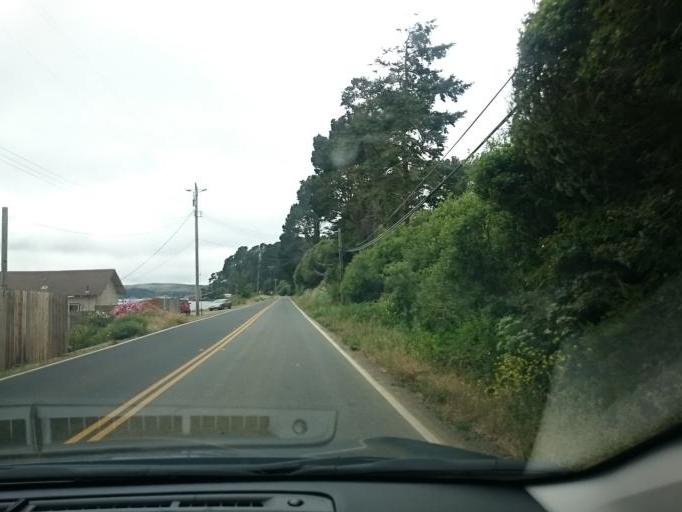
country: US
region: California
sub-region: Marin County
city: Inverness
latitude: 38.1415
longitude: -122.8741
